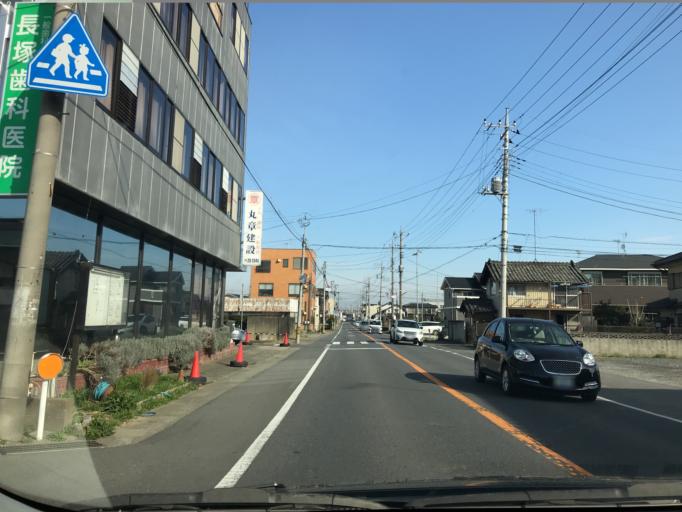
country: JP
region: Ibaraki
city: Mitsukaido
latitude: 36.0263
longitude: 139.9933
